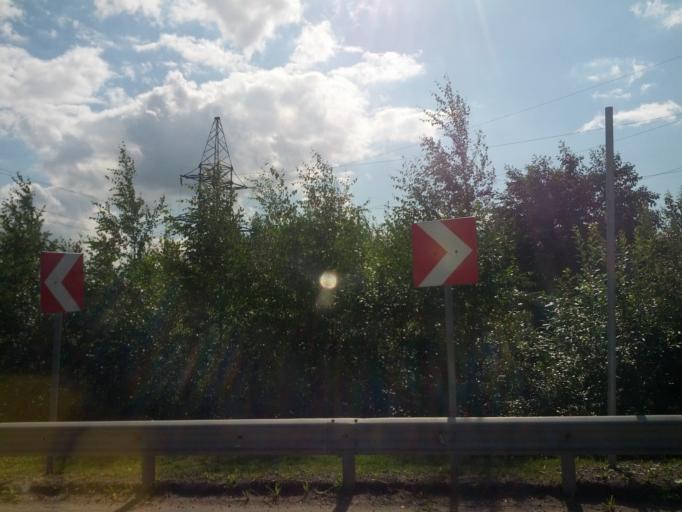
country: RU
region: Leningrad
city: Rybatskoye
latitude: 59.8856
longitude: 30.5069
